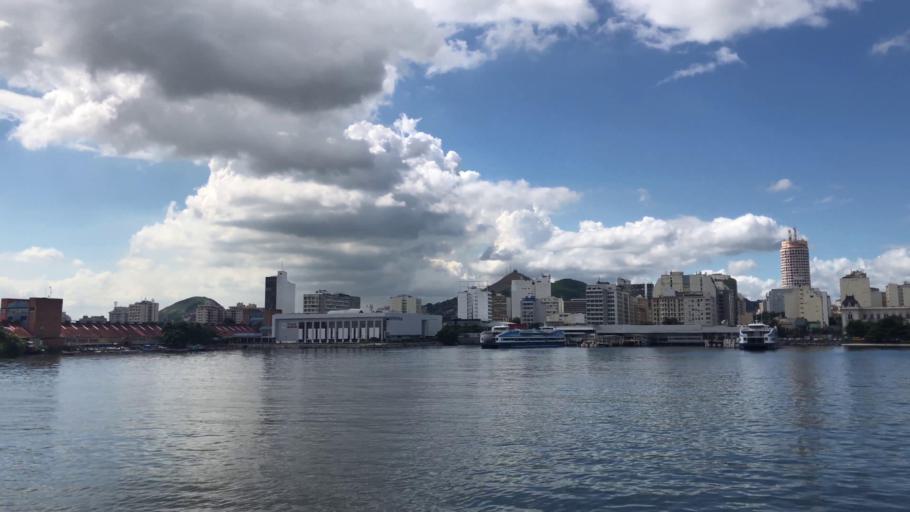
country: BR
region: Rio de Janeiro
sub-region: Niteroi
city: Niteroi
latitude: -22.8929
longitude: -43.1264
